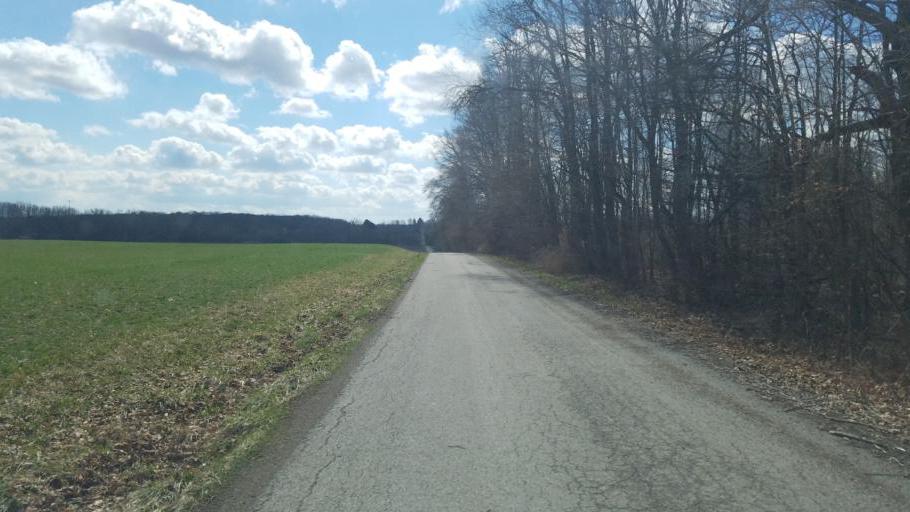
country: US
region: Ohio
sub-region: Knox County
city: Fredericktown
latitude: 40.5100
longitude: -82.5709
